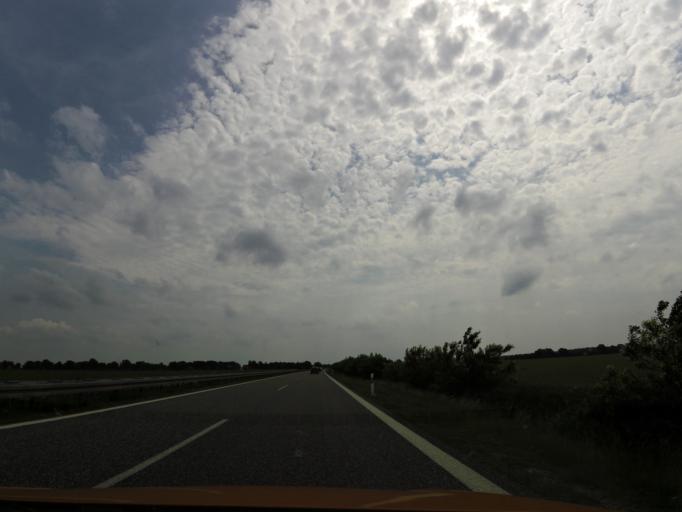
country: DE
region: Mecklenburg-Vorpommern
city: Mirow
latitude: 53.4753
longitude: 11.4906
